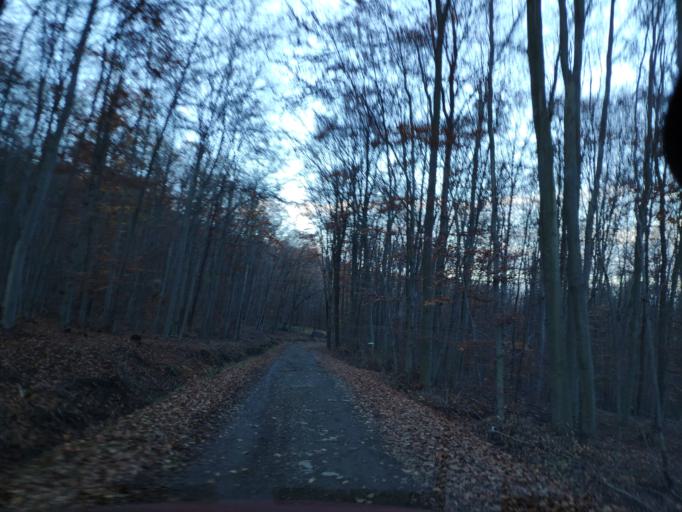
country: SK
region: Kosicky
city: Secovce
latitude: 48.5885
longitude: 21.5063
